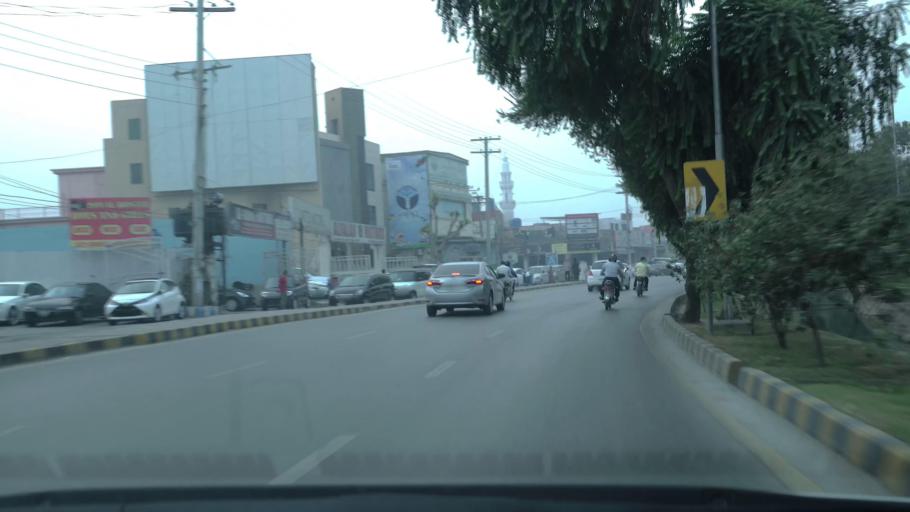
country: PK
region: Punjab
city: Lahore
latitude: 31.4707
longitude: 74.3030
